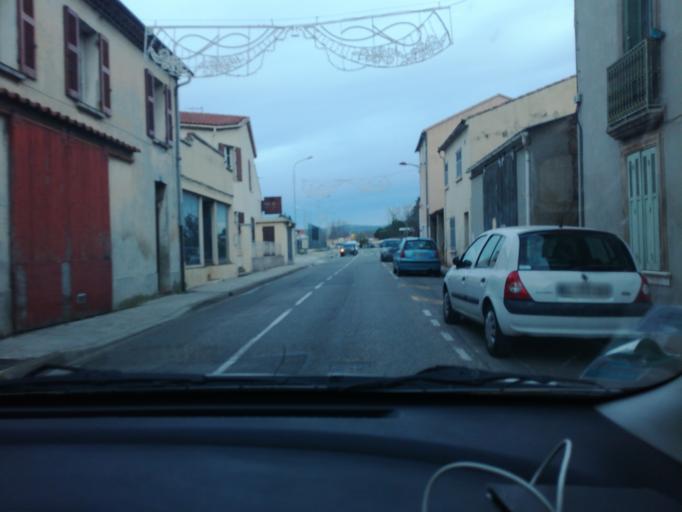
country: FR
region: Provence-Alpes-Cote d'Azur
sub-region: Departement du Var
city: La Crau
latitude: 43.1505
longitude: 6.0734
